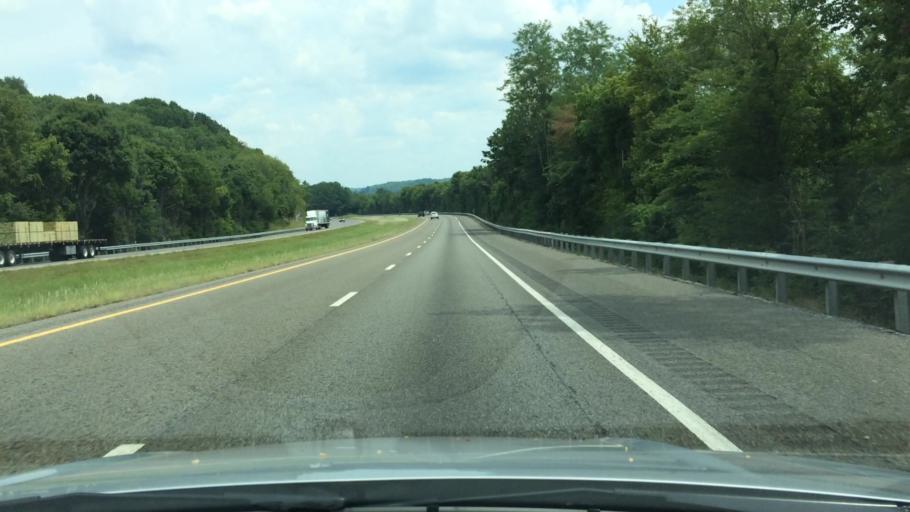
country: US
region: Tennessee
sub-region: Marshall County
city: Cornersville
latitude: 35.4112
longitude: -86.8779
